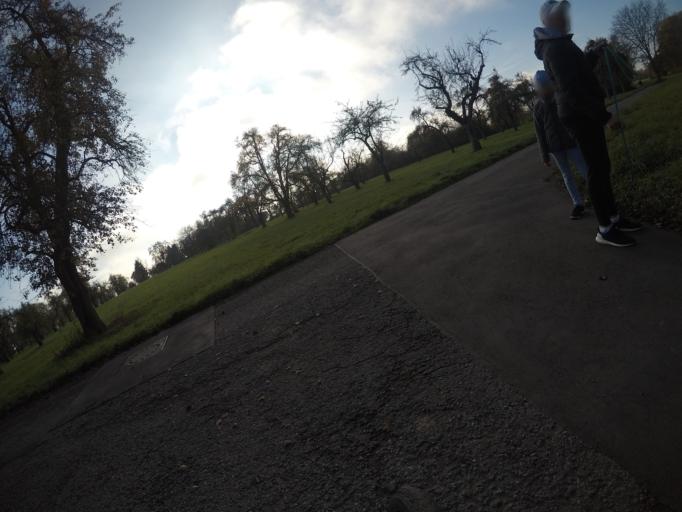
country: DE
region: Baden-Wuerttemberg
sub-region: Regierungsbezirk Stuttgart
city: Leinfelden-Echterdingen
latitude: 48.7248
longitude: 9.1393
